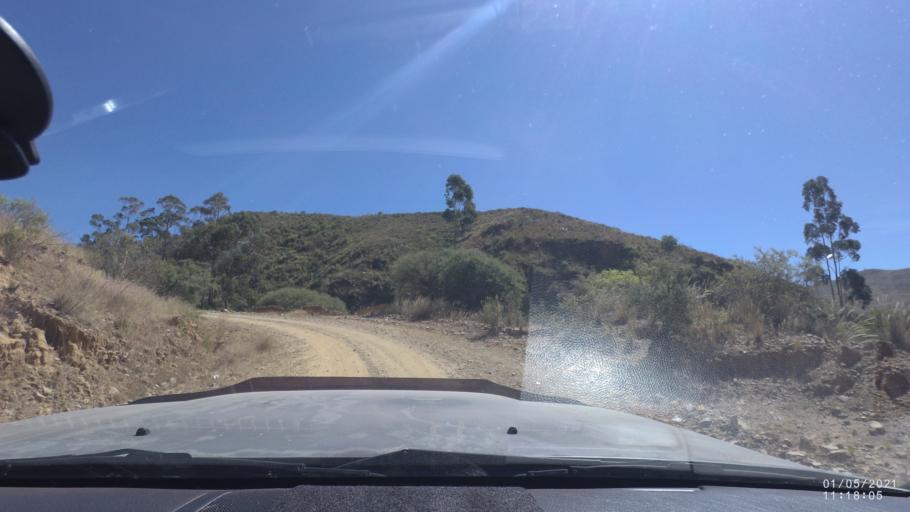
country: BO
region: Cochabamba
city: Tarata
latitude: -17.6405
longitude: -66.1160
